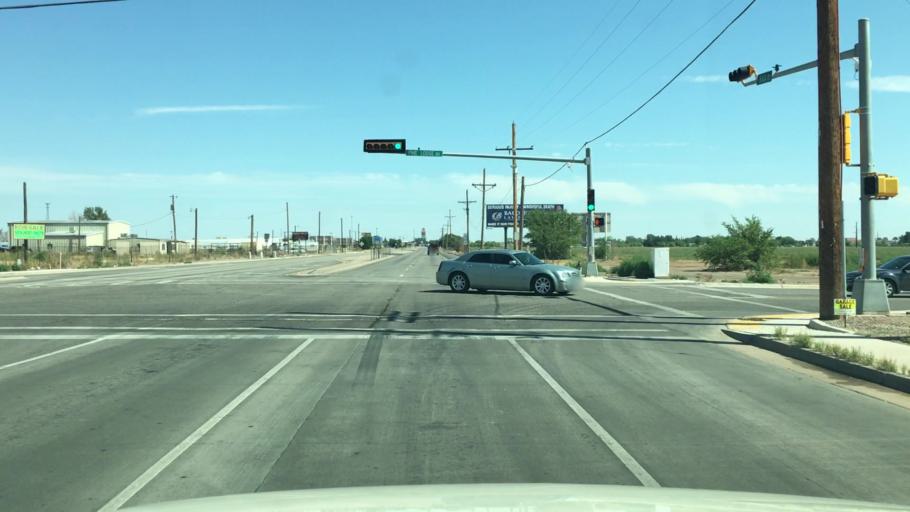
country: US
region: New Mexico
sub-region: Chaves County
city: Roswell
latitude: 33.4521
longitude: -104.5233
